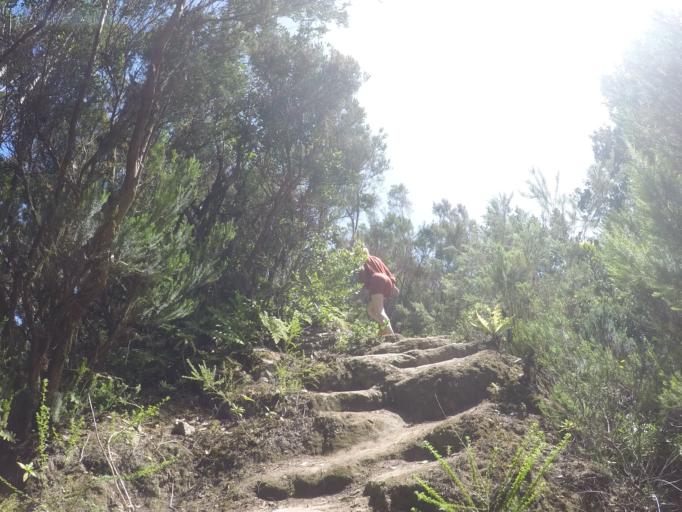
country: ES
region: Canary Islands
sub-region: Provincia de Santa Cruz de Tenerife
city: Santa Cruz de Tenerife
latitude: 28.5447
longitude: -16.2266
